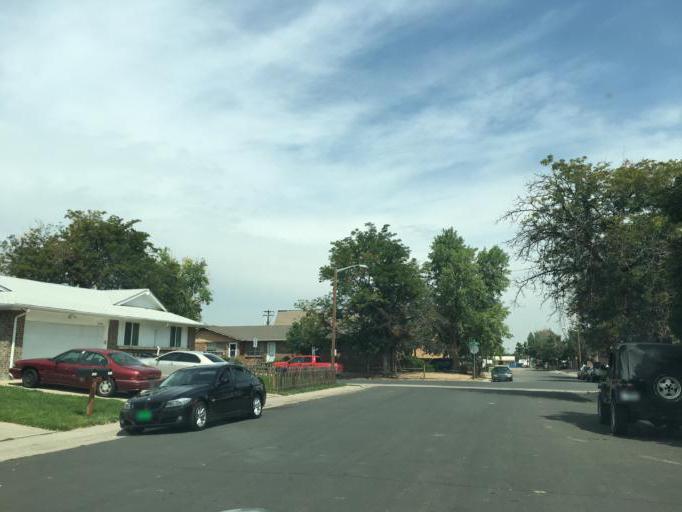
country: US
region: Colorado
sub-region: Adams County
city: Aurora
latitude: 39.7370
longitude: -104.8060
